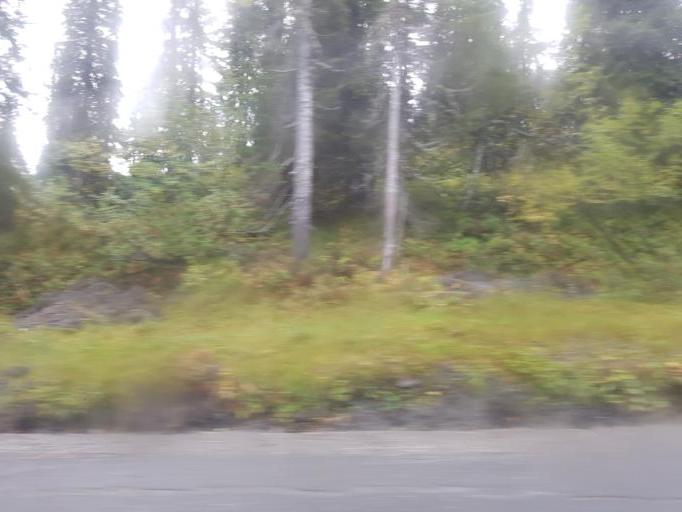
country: NO
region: Sor-Trondelag
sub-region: Trondheim
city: Trondheim
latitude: 63.4147
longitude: 10.2749
